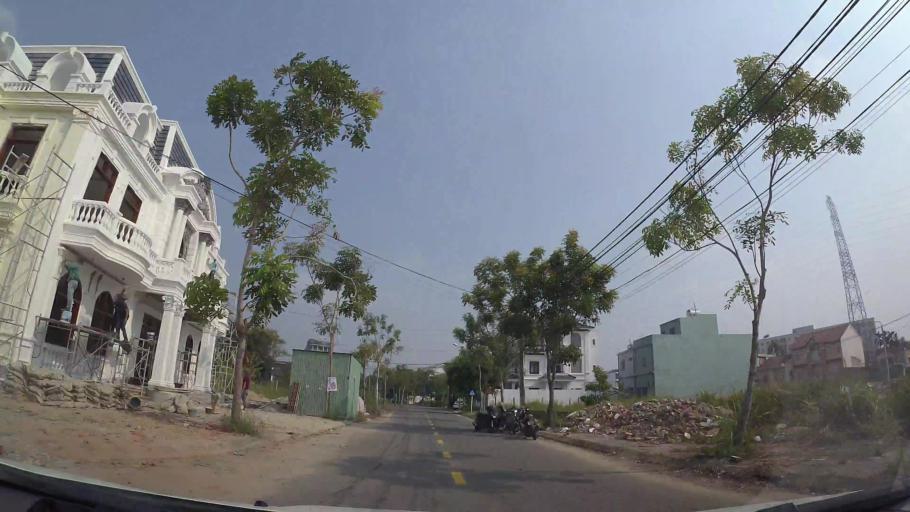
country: VN
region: Da Nang
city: Ngu Hanh Son
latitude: 16.0342
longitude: 108.2406
